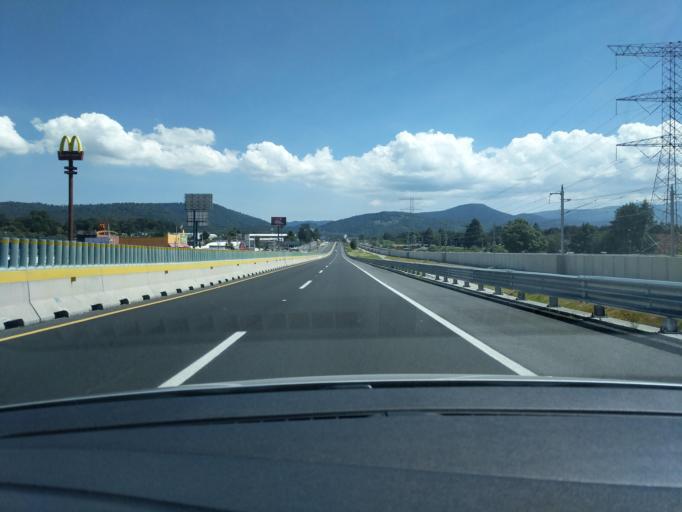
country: MX
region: Morelos
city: Ocoyoacac
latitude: 19.2842
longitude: -99.4594
